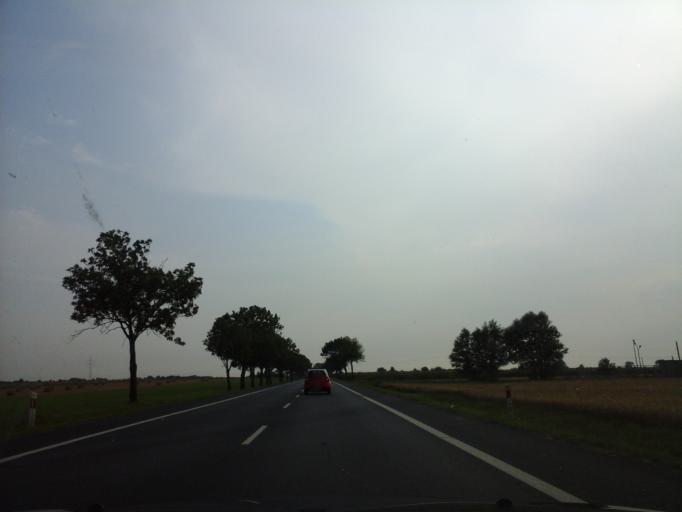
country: PL
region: Greater Poland Voivodeship
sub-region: Powiat koscianski
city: Koscian
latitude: 52.0688
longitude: 16.6100
